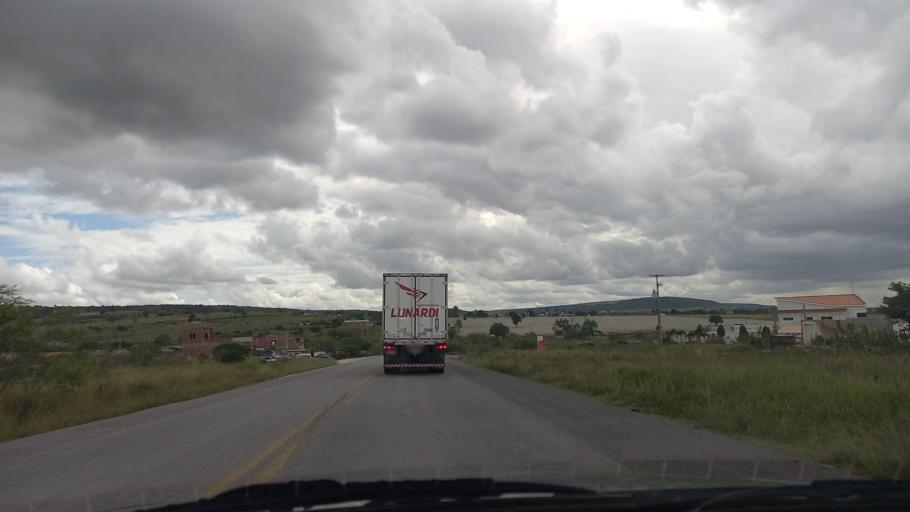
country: BR
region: Pernambuco
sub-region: Lajedo
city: Lajedo
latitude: -8.6643
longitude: -36.3567
